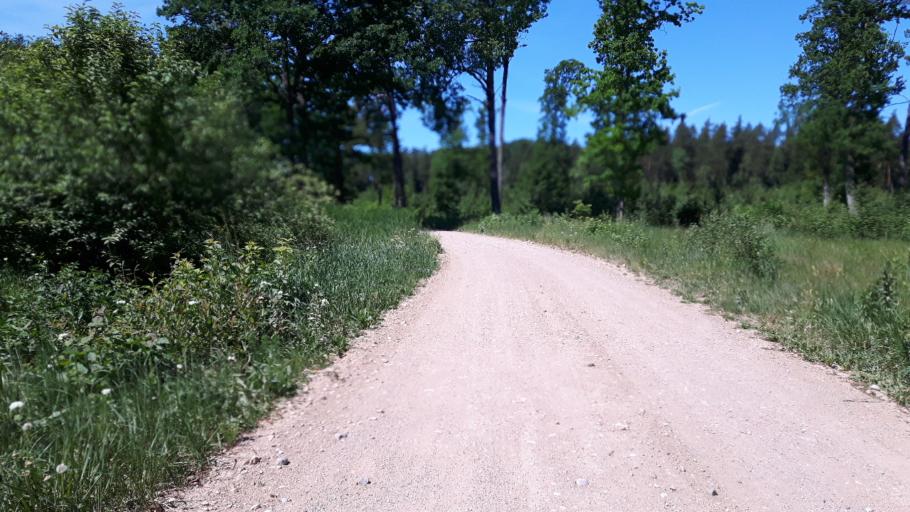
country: LV
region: Kandava
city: Kandava
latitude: 57.0427
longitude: 22.8524
